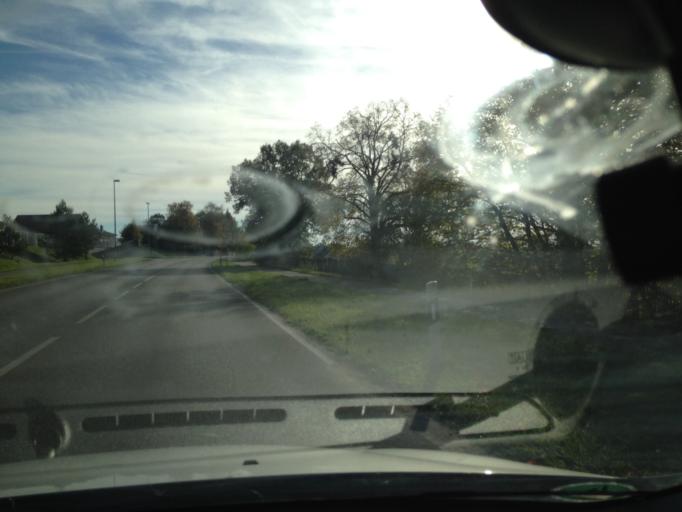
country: DE
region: Bavaria
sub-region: Swabia
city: Bobingen
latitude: 48.2848
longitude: 10.8442
